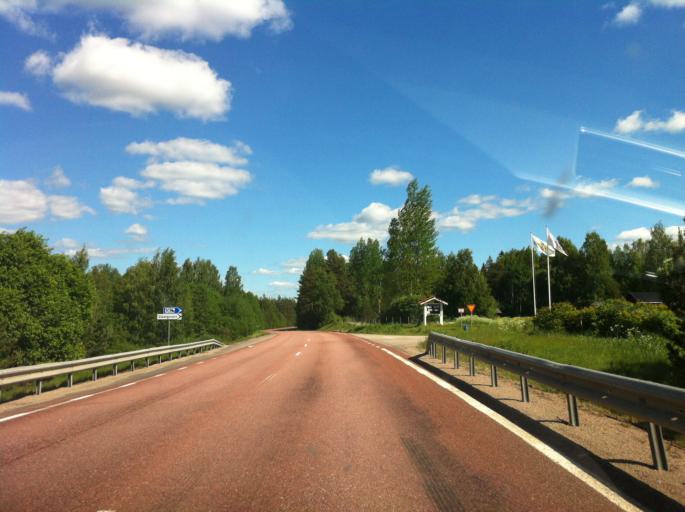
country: SE
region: Gaevleborg
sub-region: Ljusdals Kommun
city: Farila
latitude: 61.9290
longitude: 15.5554
